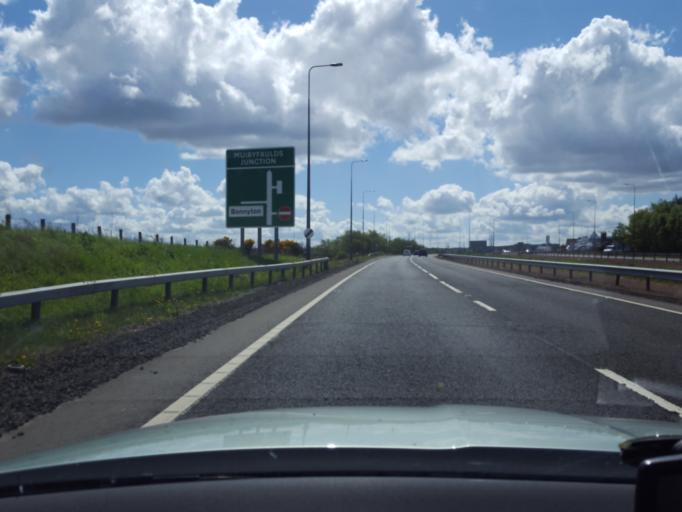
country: GB
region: Scotland
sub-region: Angus
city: Forfar
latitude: 56.5774
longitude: -2.9134
